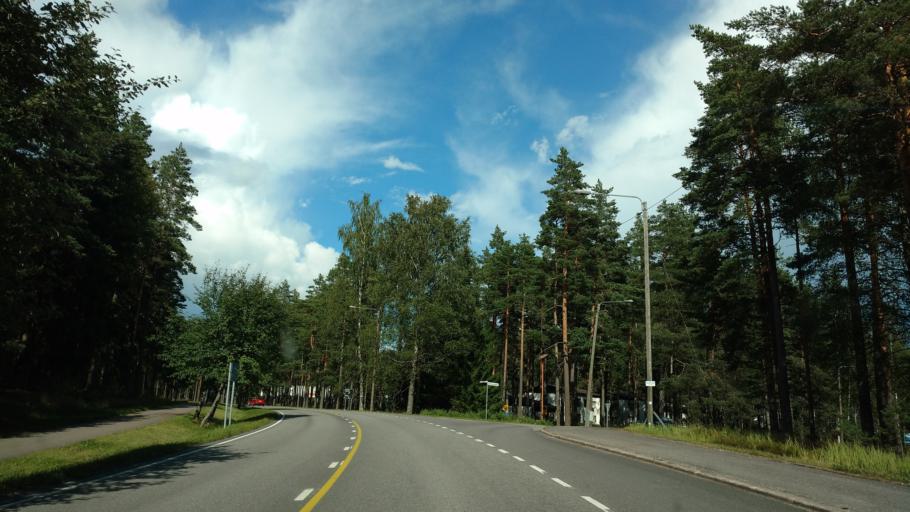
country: FI
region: Varsinais-Suomi
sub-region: Turku
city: Paimio
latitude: 60.4625
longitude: 22.7309
